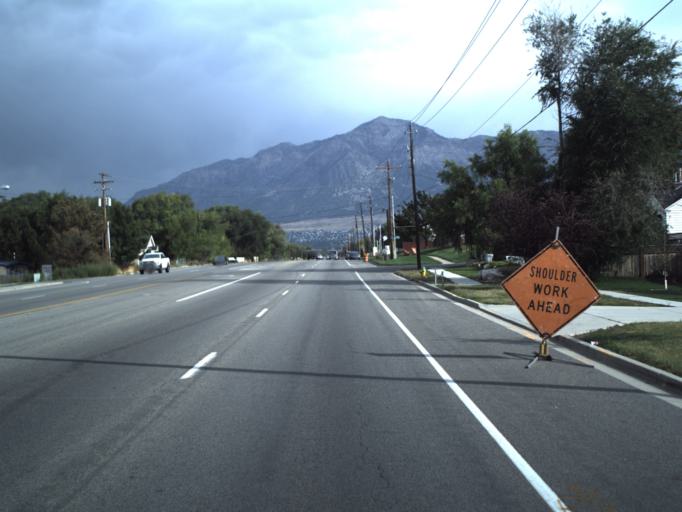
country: US
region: Utah
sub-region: Weber County
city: Harrisville
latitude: 41.2689
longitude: -111.9694
